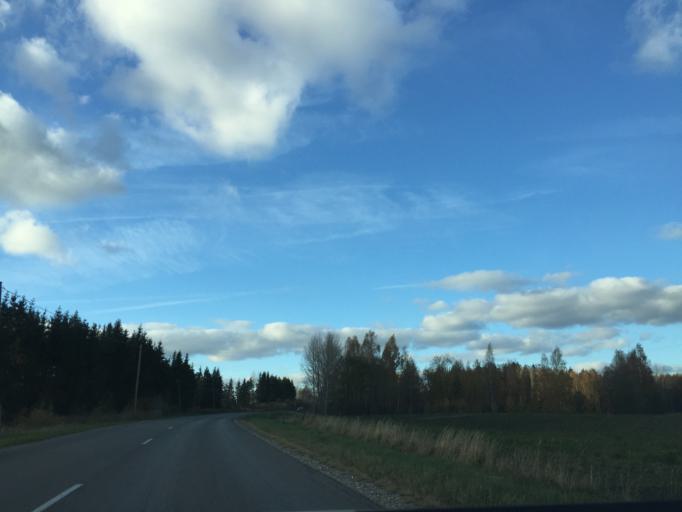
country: LV
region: Tukuma Rajons
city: Tukums
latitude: 56.9749
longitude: 23.1217
